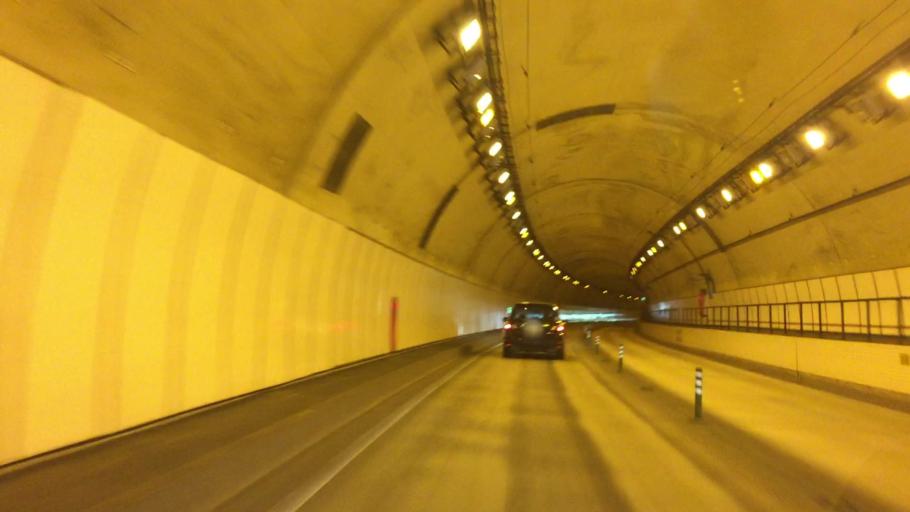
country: JP
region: Saitama
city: Yorii
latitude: 36.1053
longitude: 139.1549
